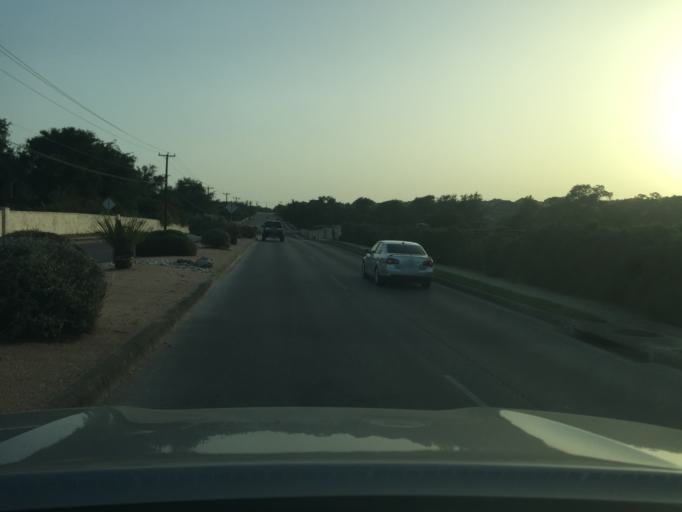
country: US
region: Texas
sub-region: Bexar County
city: Timberwood Park
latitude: 29.6659
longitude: -98.4867
